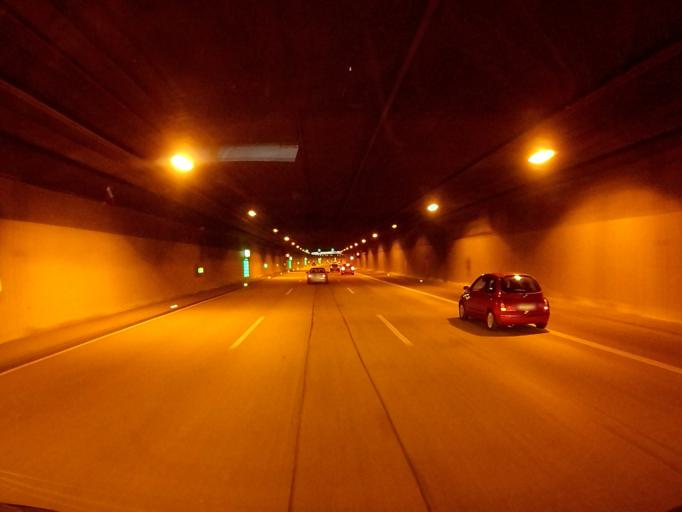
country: DE
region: North Rhine-Westphalia
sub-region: Regierungsbezirk Dusseldorf
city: Dusseldorf
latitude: 51.1925
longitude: 6.7928
